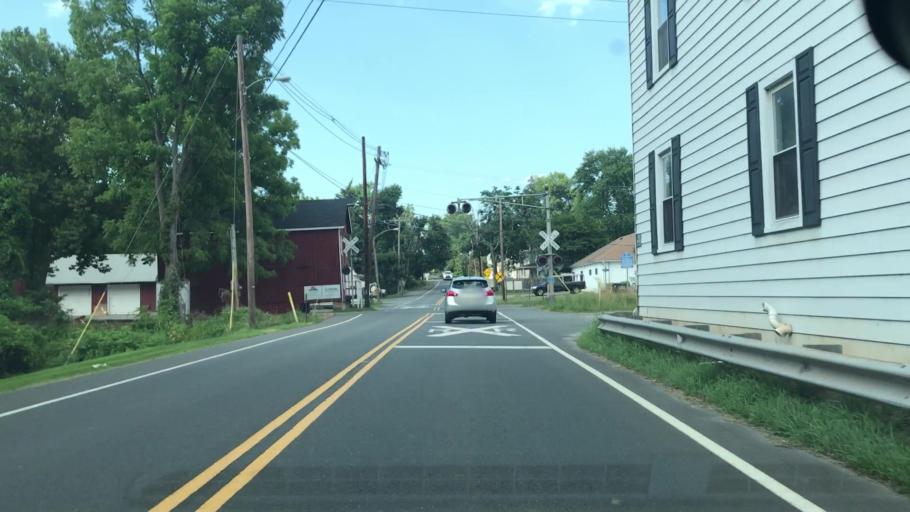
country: US
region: New Jersey
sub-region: Hunterdon County
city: Flemington
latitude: 40.5184
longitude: -74.8007
